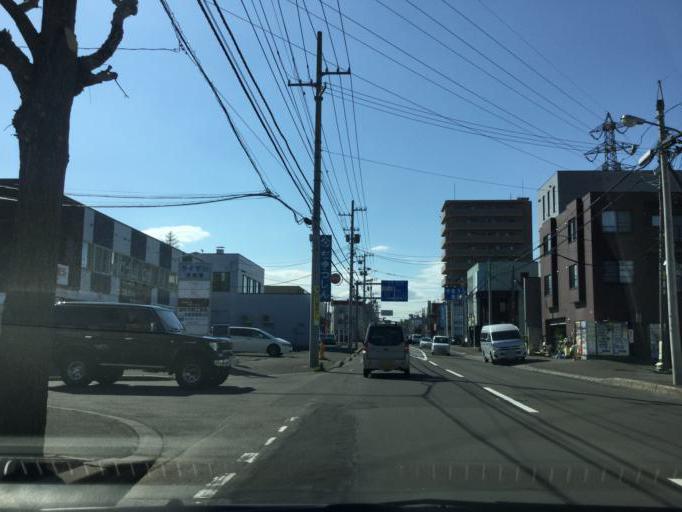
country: JP
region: Hokkaido
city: Sapporo
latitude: 43.0253
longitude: 141.4358
